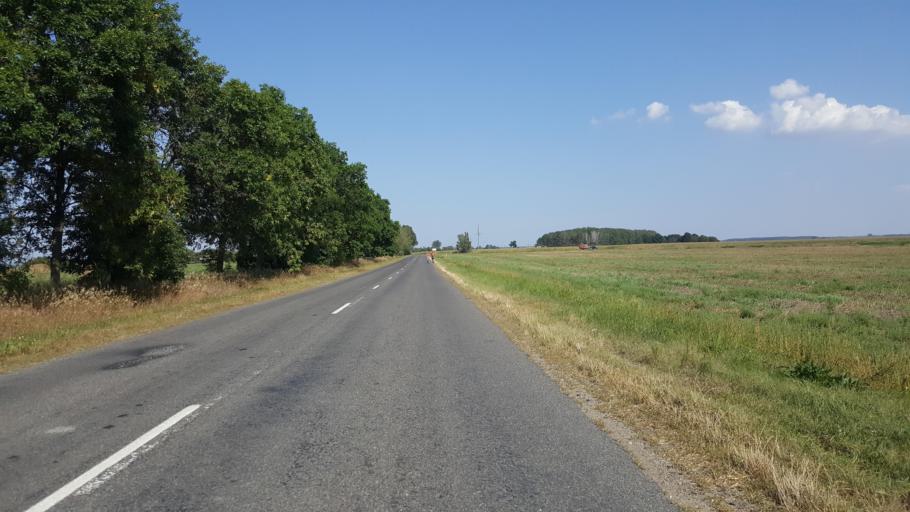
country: PL
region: Podlasie
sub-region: Powiat hajnowski
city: Czeremcha
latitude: 52.4847
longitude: 23.5426
